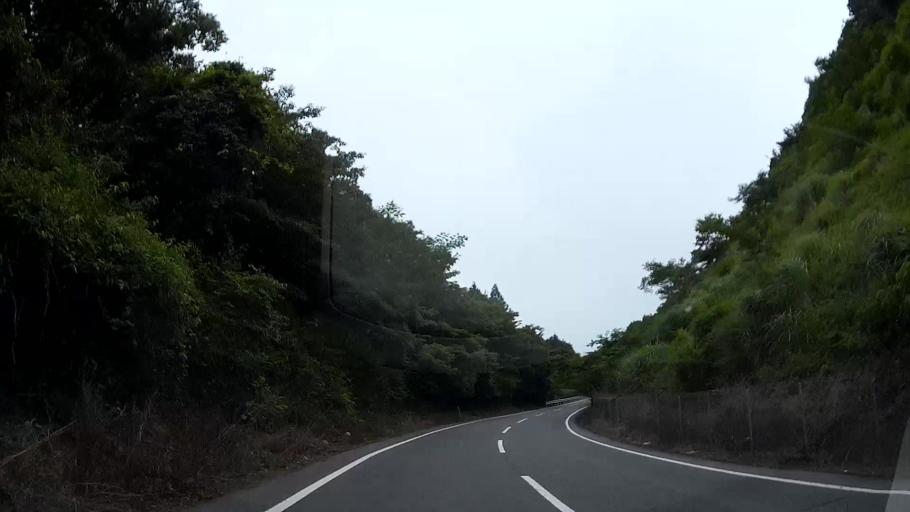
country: JP
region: Kumamoto
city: Kikuchi
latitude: 33.0595
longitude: 130.9049
